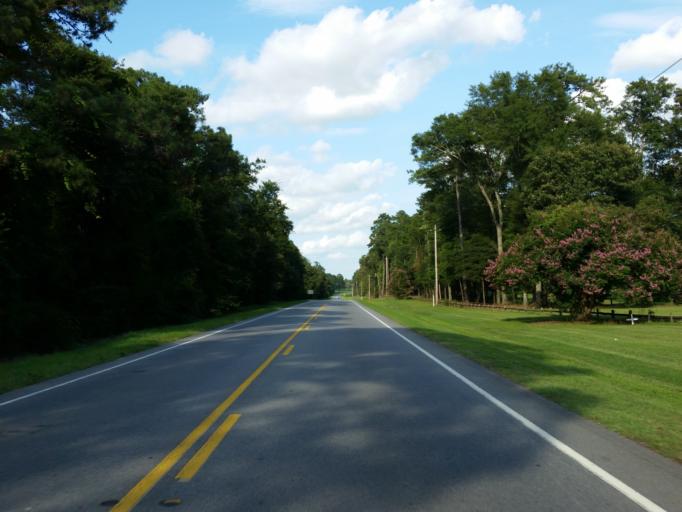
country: US
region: Georgia
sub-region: Crisp County
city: Cordele
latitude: 31.9685
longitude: -83.9092
